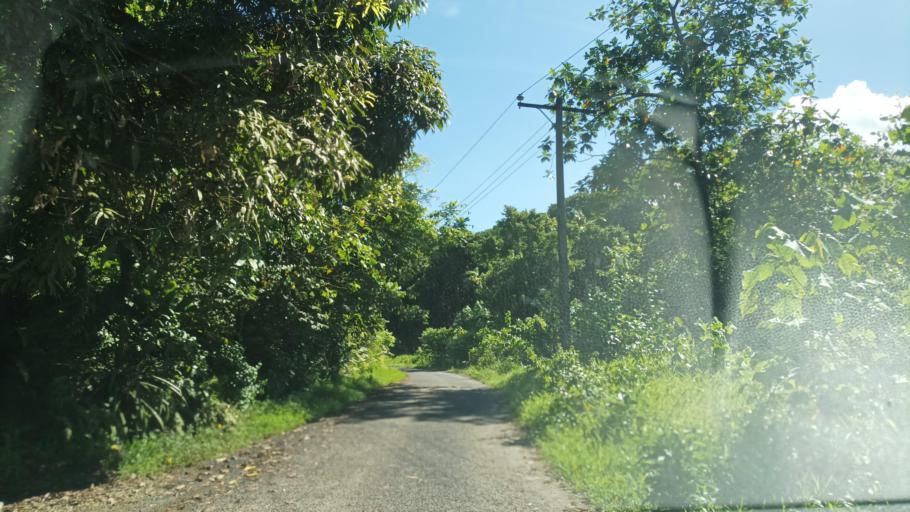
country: FM
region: Pohnpei
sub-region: Madolenihm Municipality
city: Madolenihm Municipality Government
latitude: 6.8478
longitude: 158.3164
